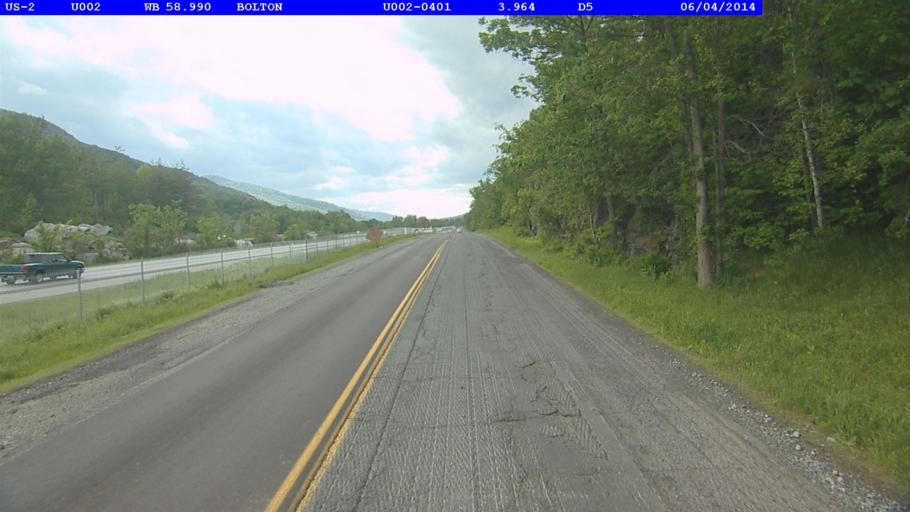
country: US
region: Vermont
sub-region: Washington County
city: Waterbury
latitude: 44.3674
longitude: -72.8577
